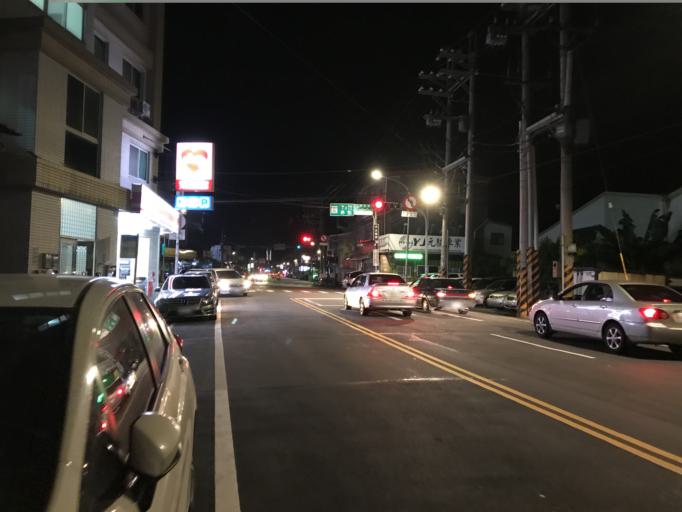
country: TW
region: Taiwan
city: Daxi
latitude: 24.9197
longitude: 121.3667
